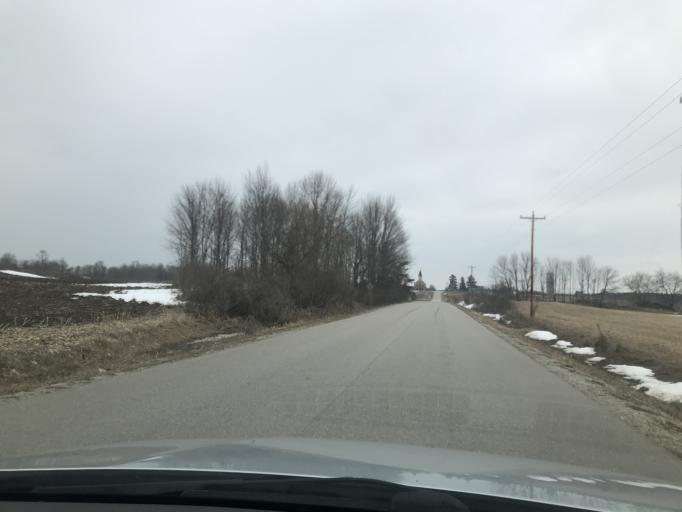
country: US
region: Wisconsin
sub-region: Marinette County
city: Peshtigo
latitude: 45.0270
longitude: -87.8787
